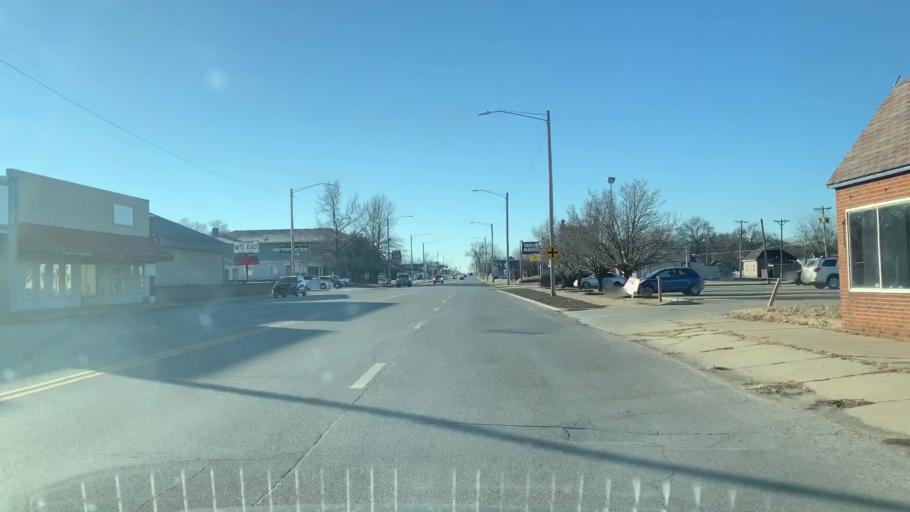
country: US
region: Kansas
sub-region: Crawford County
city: Pittsburg
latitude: 37.4061
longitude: -94.7050
